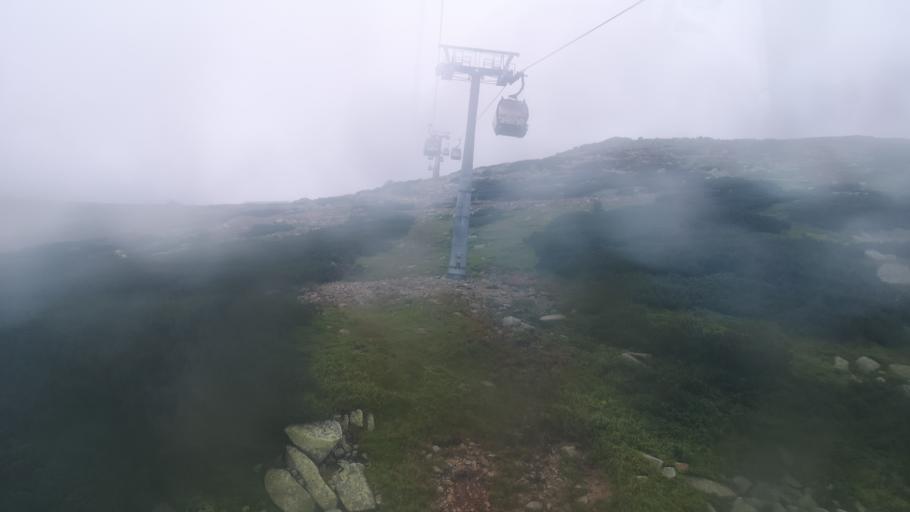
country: SK
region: Banskobystricky
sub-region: Okres Banska Bystrica
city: Brezno
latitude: 48.9383
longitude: 19.5945
